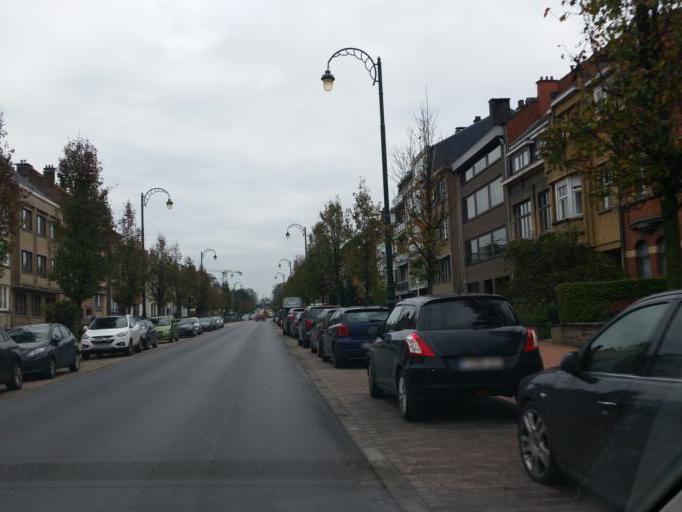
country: BE
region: Flanders
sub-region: Provincie Vlaams-Brabant
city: Wemmel
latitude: 50.9026
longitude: 4.3159
